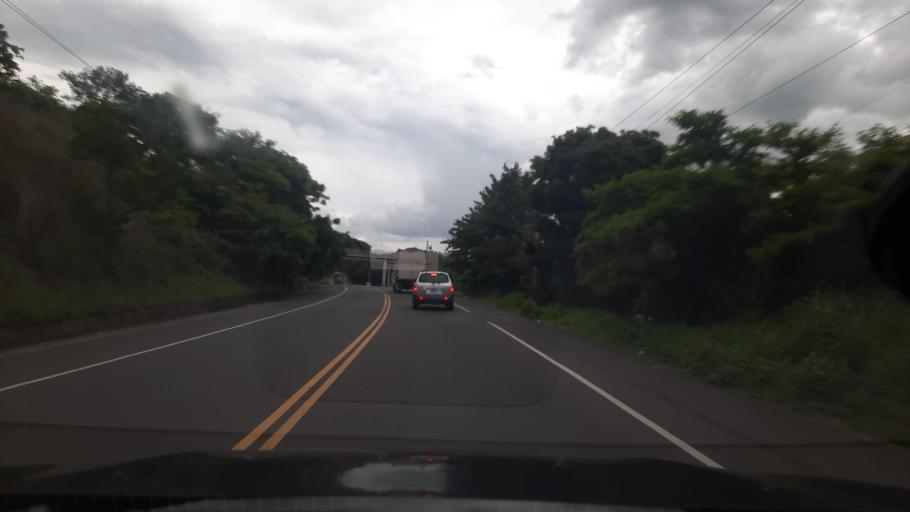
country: HN
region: Choluteca
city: Marcovia
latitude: 13.3573
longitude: -87.2760
